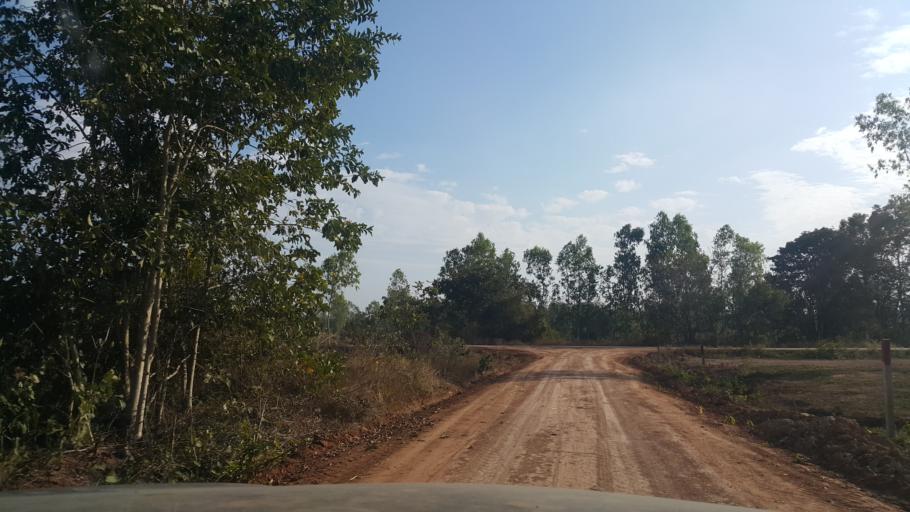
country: TH
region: Lampang
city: Hang Chat
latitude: 18.2747
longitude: 99.3562
